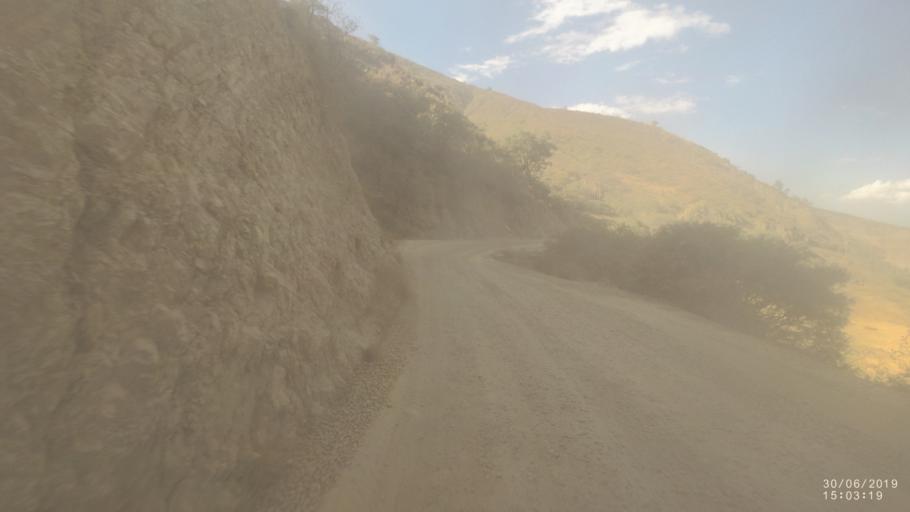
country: BO
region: Cochabamba
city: Irpa Irpa
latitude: -17.7318
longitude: -66.3276
